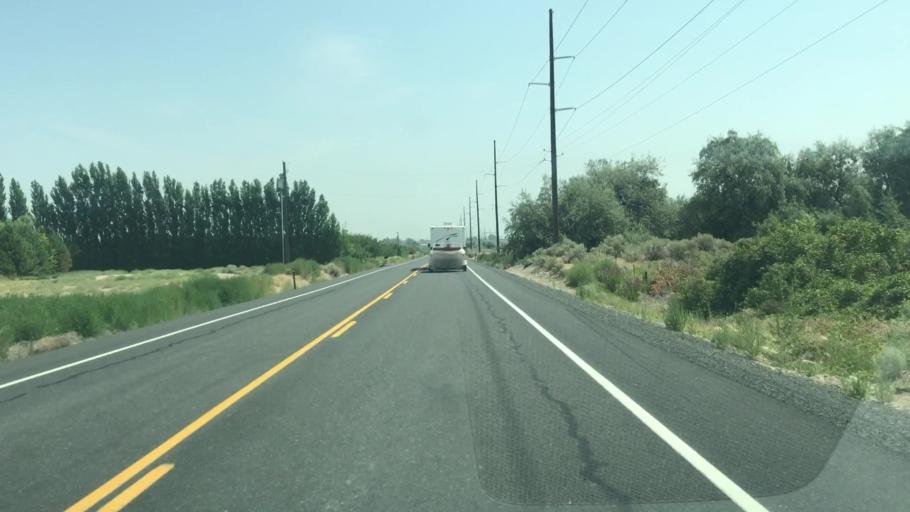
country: US
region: Washington
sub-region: Grant County
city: Quincy
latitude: 47.1602
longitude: -119.9111
